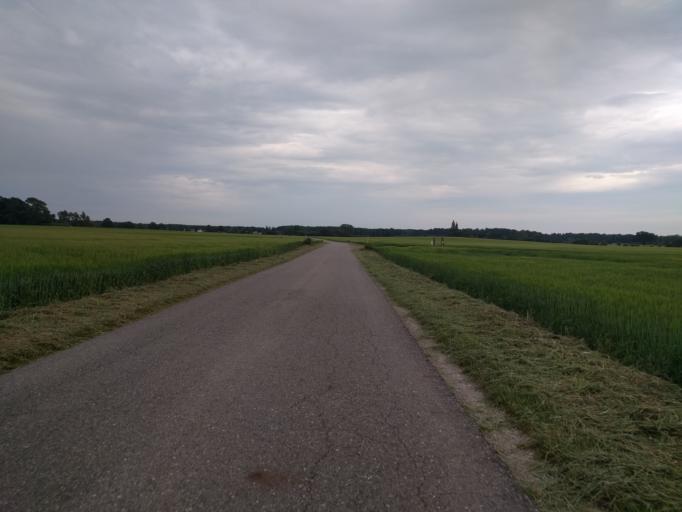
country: DK
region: South Denmark
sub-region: Kerteminde Kommune
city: Kerteminde
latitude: 55.4400
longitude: 10.6154
